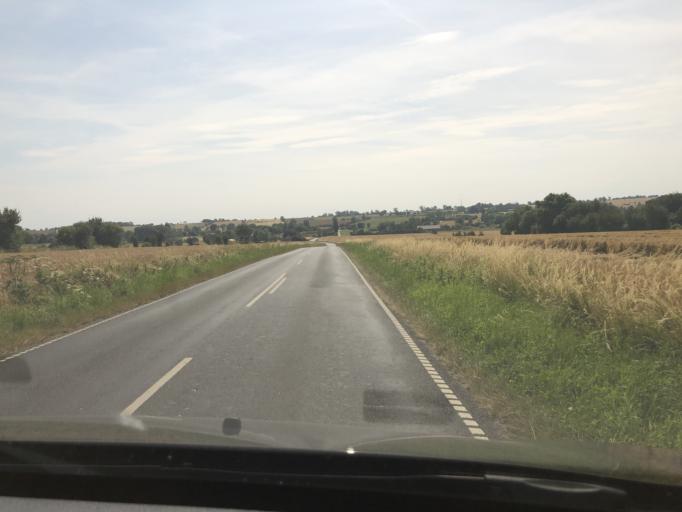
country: DK
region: South Denmark
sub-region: AEro Kommune
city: AEroskobing
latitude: 54.8777
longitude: 10.3995
